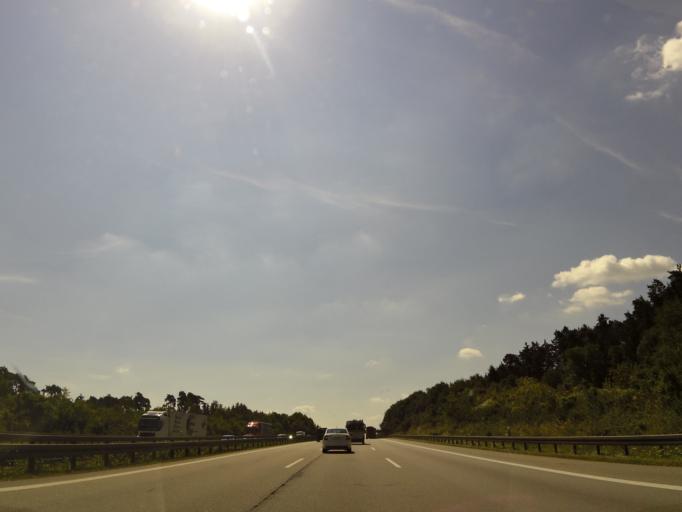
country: DE
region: Bavaria
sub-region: Upper Bavaria
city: Rohrbach
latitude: 48.6126
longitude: 11.5406
